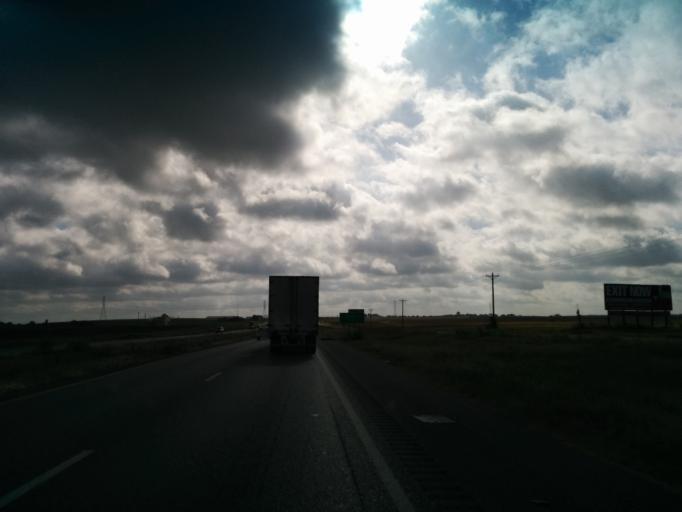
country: US
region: Texas
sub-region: Guadalupe County
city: Marion
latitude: 29.5327
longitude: -98.0981
